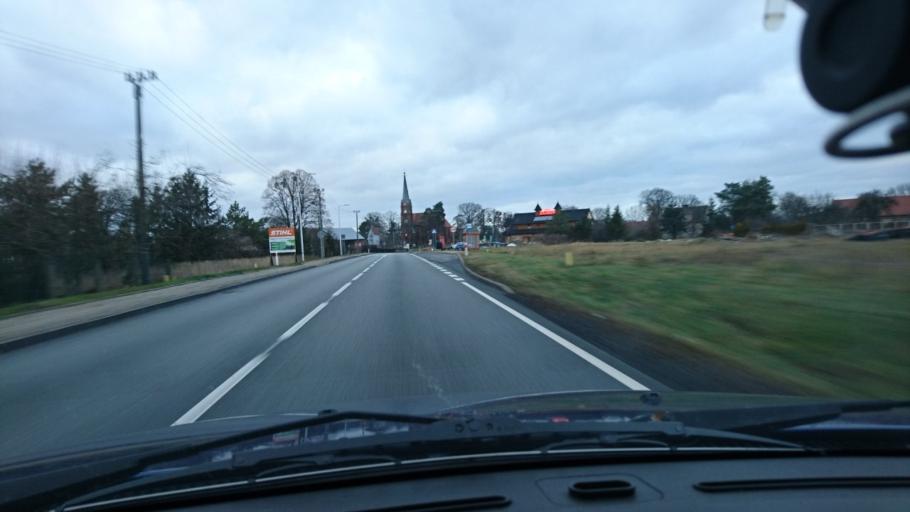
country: PL
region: Opole Voivodeship
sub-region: Powiat kluczborski
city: Kluczbork
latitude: 51.0258
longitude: 18.1926
